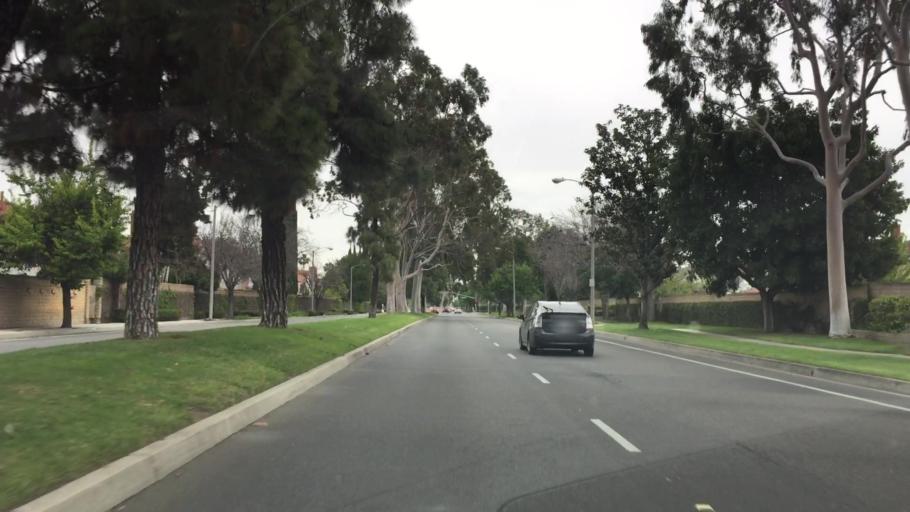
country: US
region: California
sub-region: Los Angeles County
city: Cerritos
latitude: 33.8586
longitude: -118.0581
